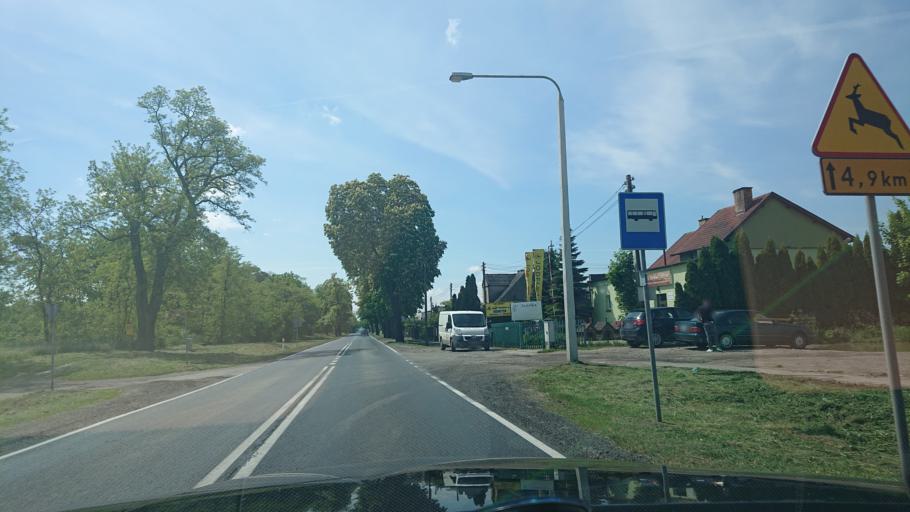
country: PL
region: Greater Poland Voivodeship
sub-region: Powiat gnieznienski
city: Gniezno
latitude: 52.5068
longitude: 17.5948
